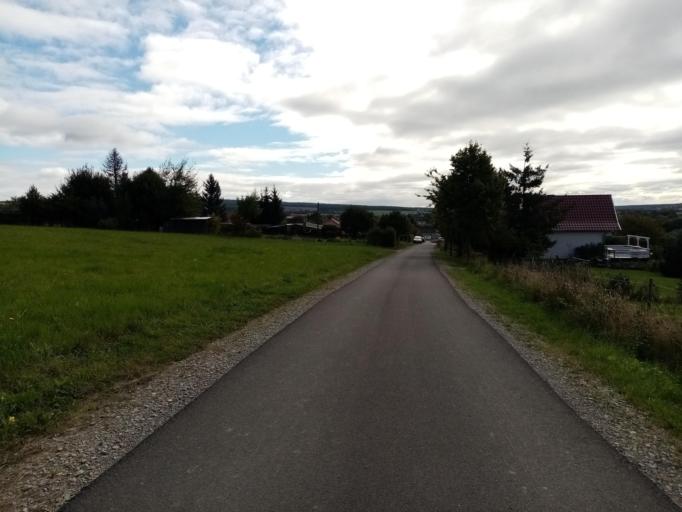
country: DE
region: Thuringia
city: Dingelstadt
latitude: 51.3209
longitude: 10.3006
